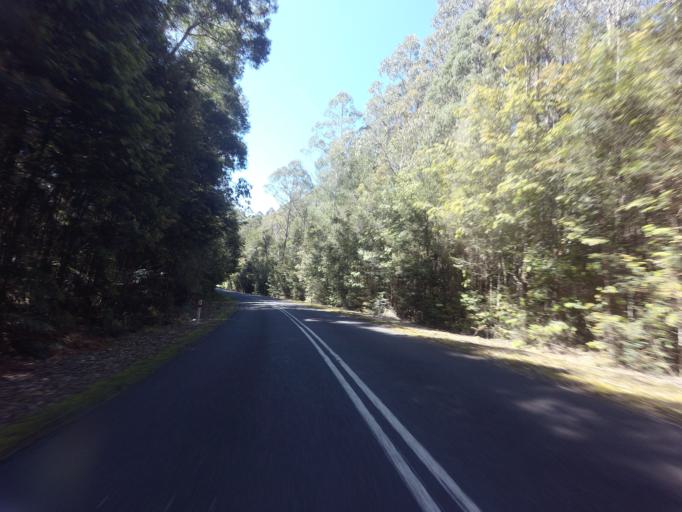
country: AU
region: Tasmania
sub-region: Huon Valley
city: Geeveston
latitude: -42.8231
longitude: 146.3327
